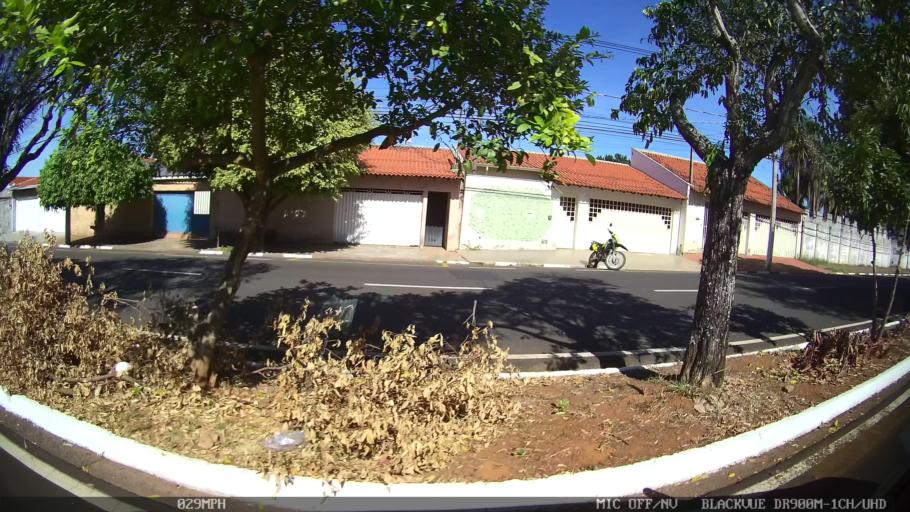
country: BR
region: Sao Paulo
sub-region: Franca
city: Franca
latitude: -20.5491
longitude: -47.3897
